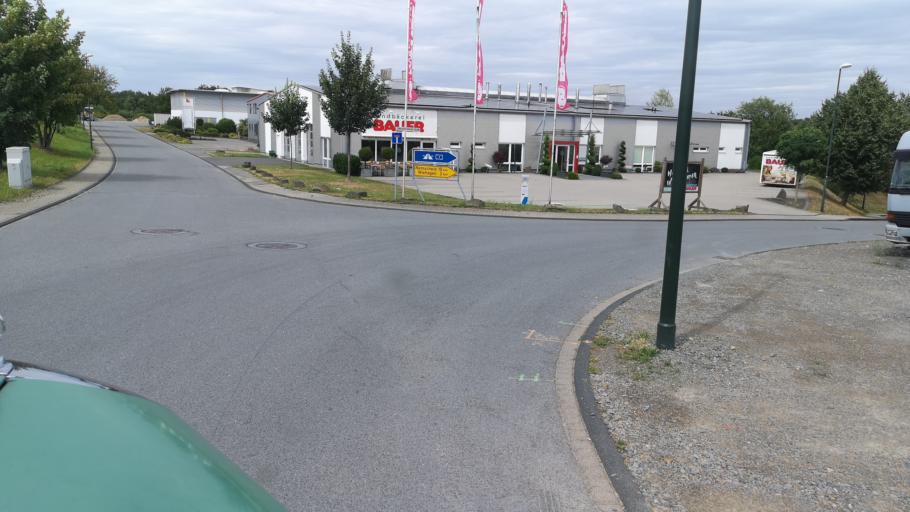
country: DE
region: North Rhine-Westphalia
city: Huckeswagen
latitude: 51.1433
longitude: 7.2965
